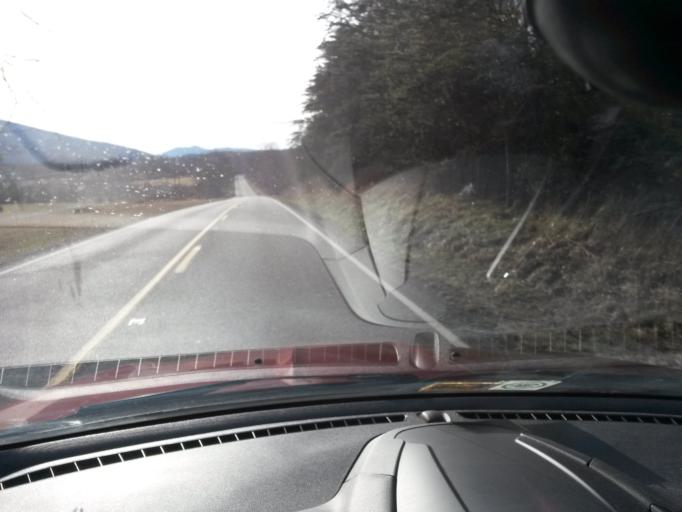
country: US
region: Virginia
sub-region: Rockbridge County
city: East Lexington
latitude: 37.9915
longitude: -79.4885
